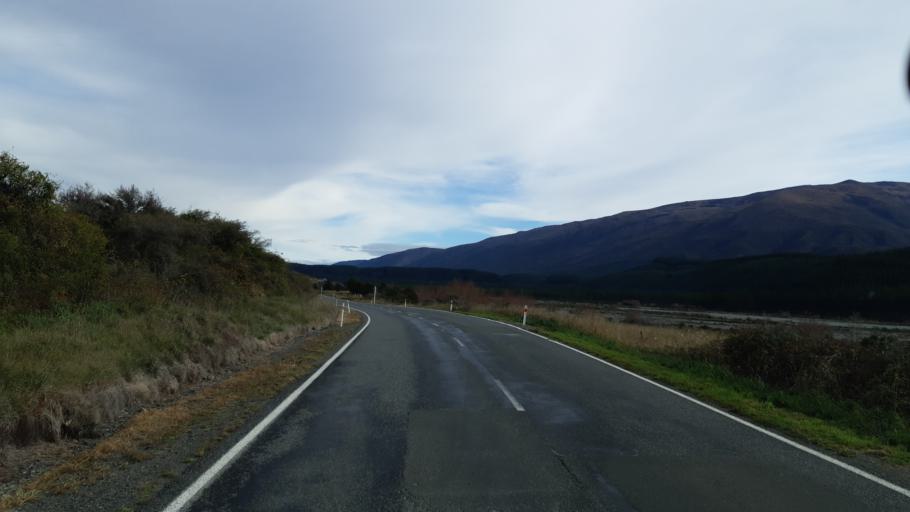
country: NZ
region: Tasman
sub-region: Tasman District
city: Wakefield
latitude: -41.6919
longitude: 173.1476
